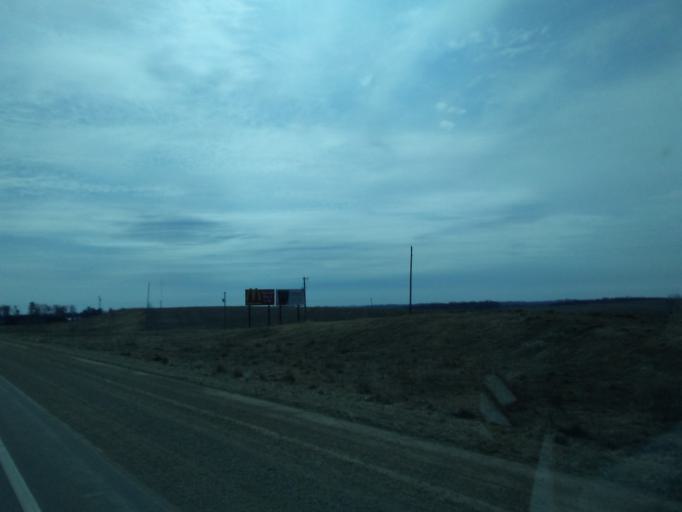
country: US
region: Iowa
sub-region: Winneshiek County
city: Decorah
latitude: 43.3596
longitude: -91.8044
